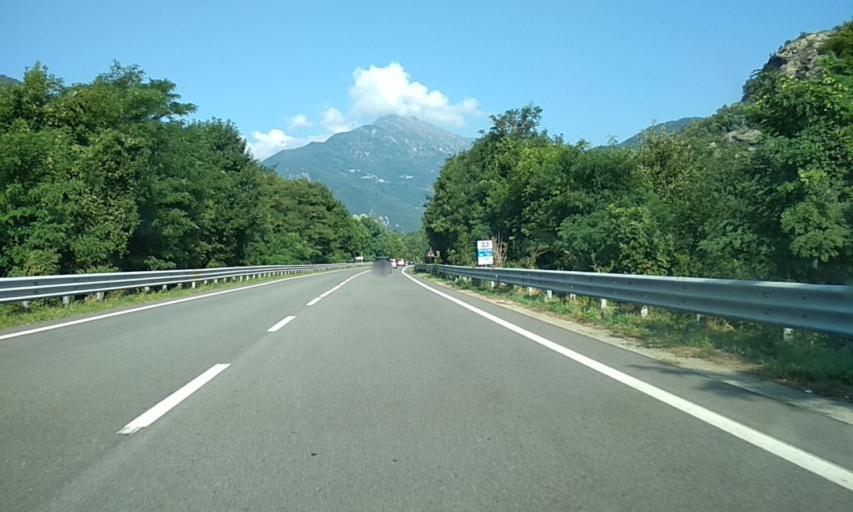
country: IT
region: Piedmont
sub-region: Provincia di Torino
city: Cuorgne
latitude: 45.4056
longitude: 7.6295
